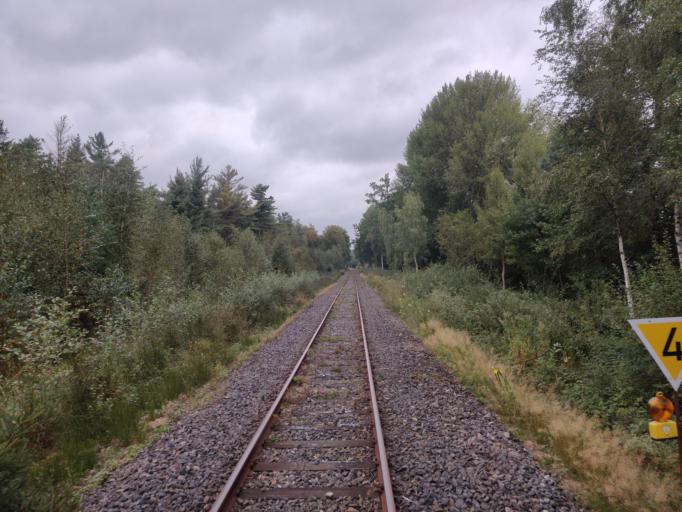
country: DE
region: Lower Saxony
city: Gnarrenburg
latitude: 53.4014
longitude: 9.0122
